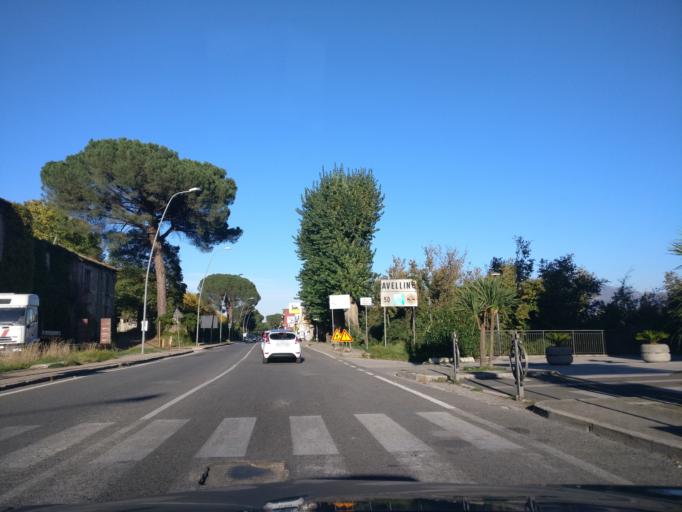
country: IT
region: Campania
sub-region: Provincia di Avellino
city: Torelli-Torrette
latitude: 40.9072
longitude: 14.7650
